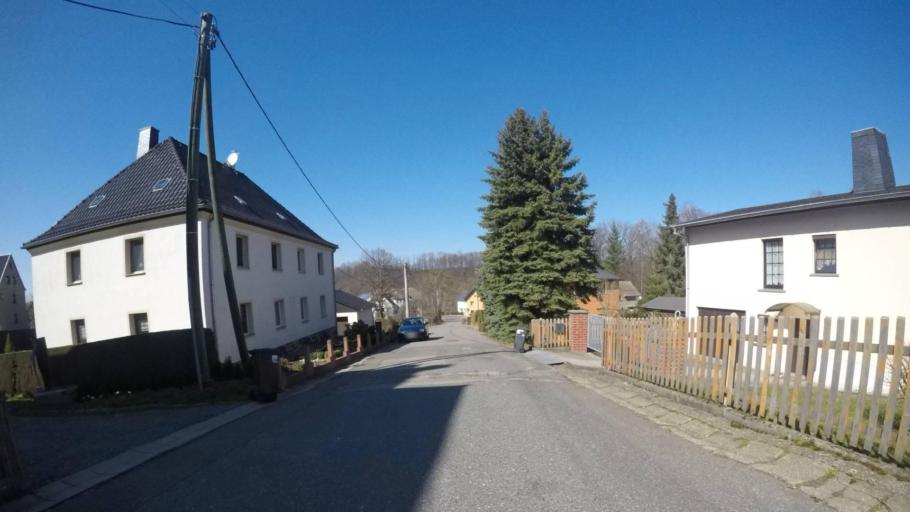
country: DE
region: Saxony
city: Niederfrohna
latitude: 50.8985
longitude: 12.6709
